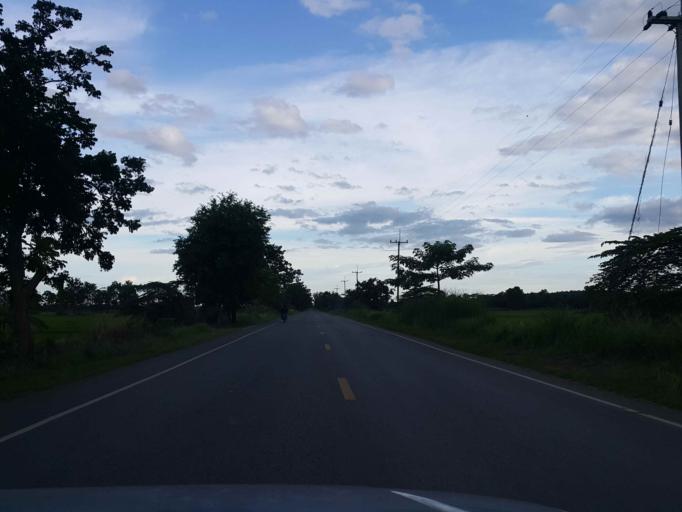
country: TH
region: Sukhothai
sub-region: Amphoe Si Satchanalai
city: Si Satchanalai
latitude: 17.4157
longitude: 99.7268
